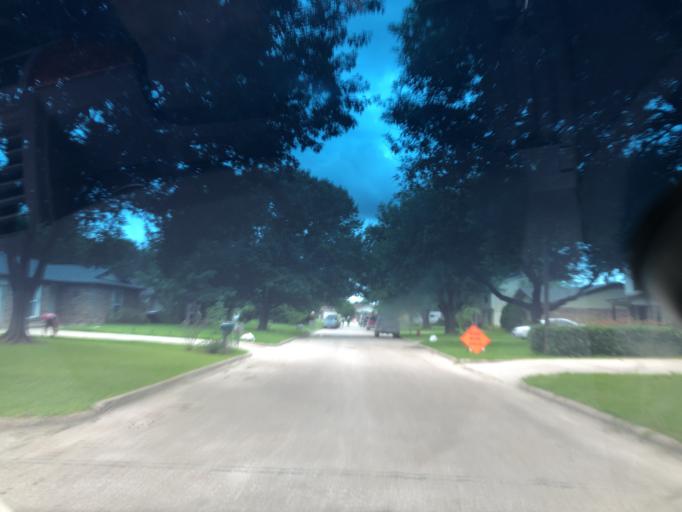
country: US
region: Texas
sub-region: Dallas County
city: Grand Prairie
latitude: 32.6953
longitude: -97.0113
